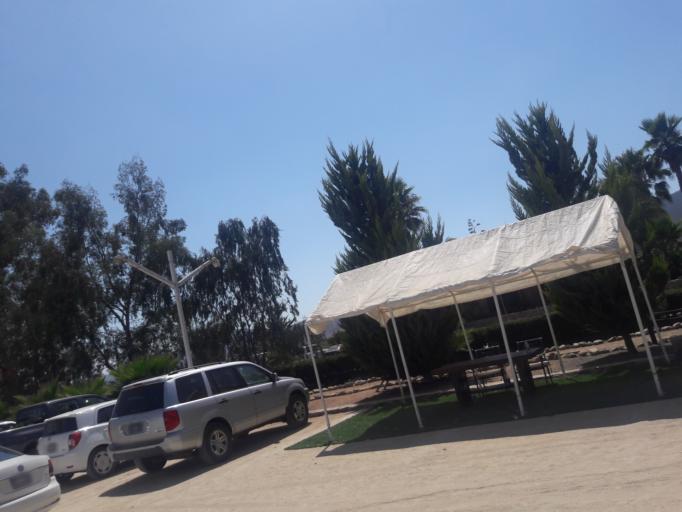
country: MX
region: Baja California
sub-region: Ensenada
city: Rancho Verde
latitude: 32.0992
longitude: -116.6218
